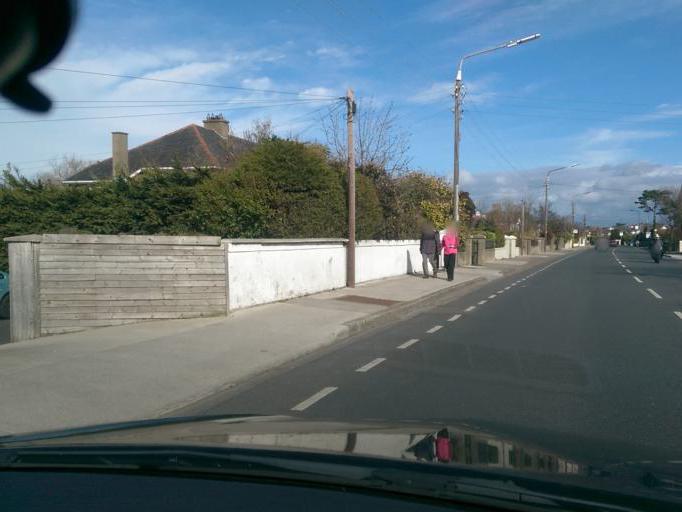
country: IE
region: Leinster
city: Sutton
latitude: 53.3898
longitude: -6.1068
